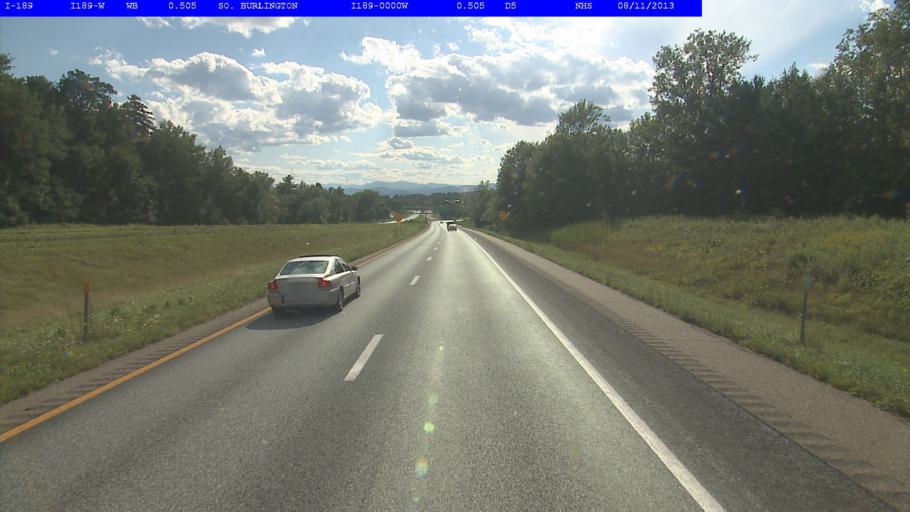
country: US
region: Vermont
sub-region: Chittenden County
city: Burlington
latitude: 44.4493
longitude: -73.2006
